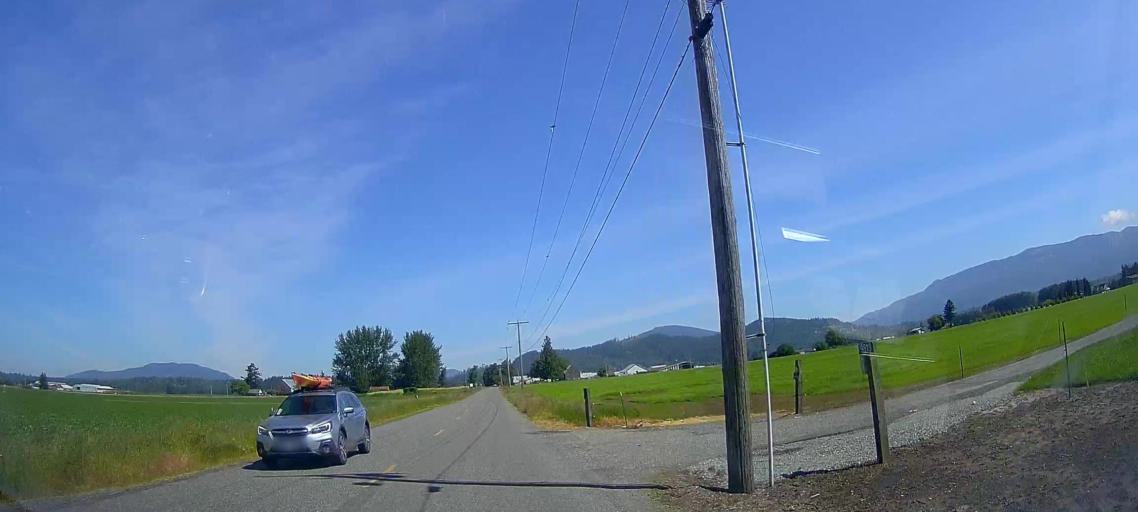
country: US
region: Washington
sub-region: Skagit County
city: Burlington
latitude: 48.5031
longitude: -122.3075
